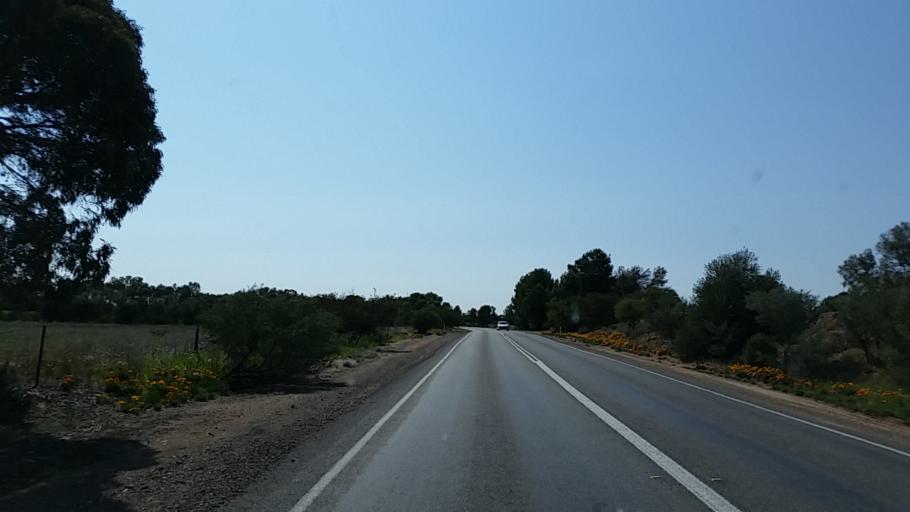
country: AU
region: South Australia
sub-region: Port Pirie City and Dists
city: Crystal Brook
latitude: -33.2645
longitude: 138.3474
